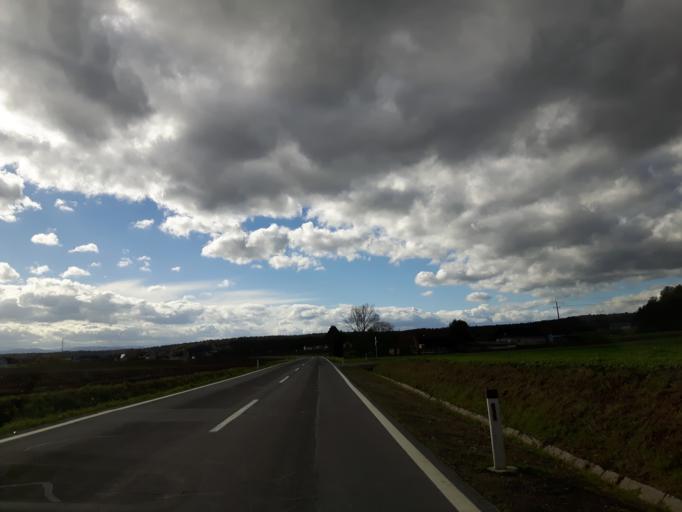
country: AT
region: Styria
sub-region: Politischer Bezirk Leibnitz
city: Breitenfeld am Tannenriegel
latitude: 46.8522
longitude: 15.6466
